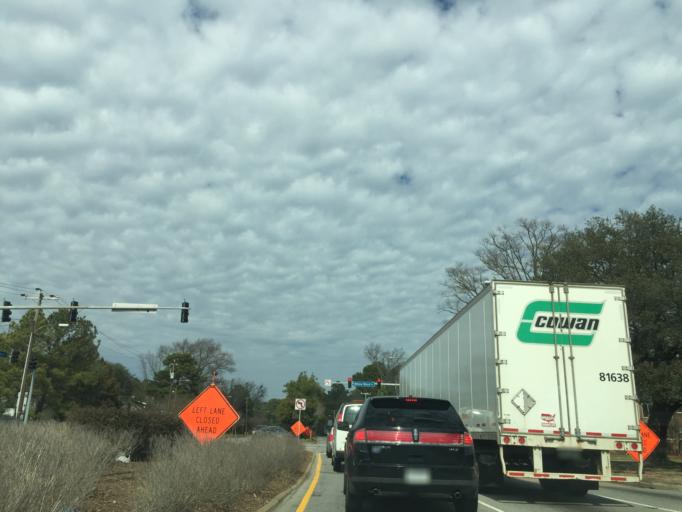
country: US
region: Virginia
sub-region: City of Norfolk
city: Norfolk
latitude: 36.8900
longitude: -76.2791
